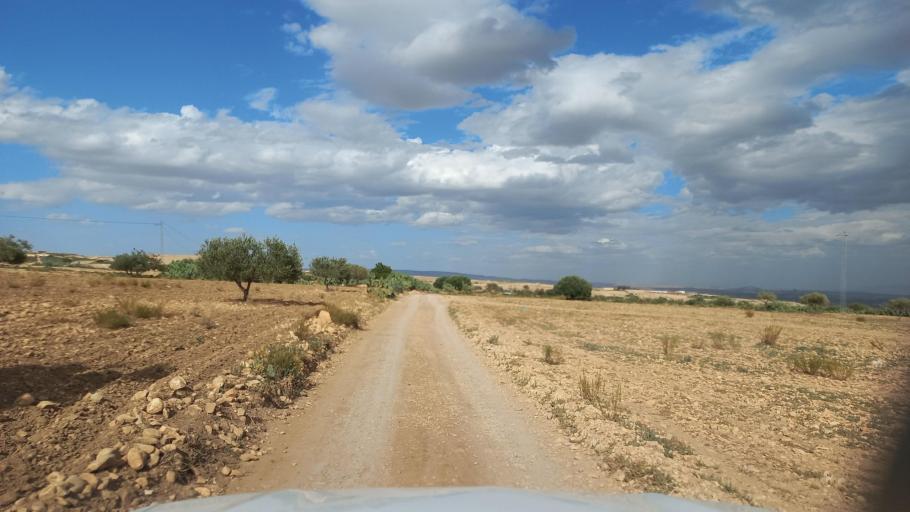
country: TN
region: Al Qasrayn
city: Sbiba
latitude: 35.4482
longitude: 9.0754
